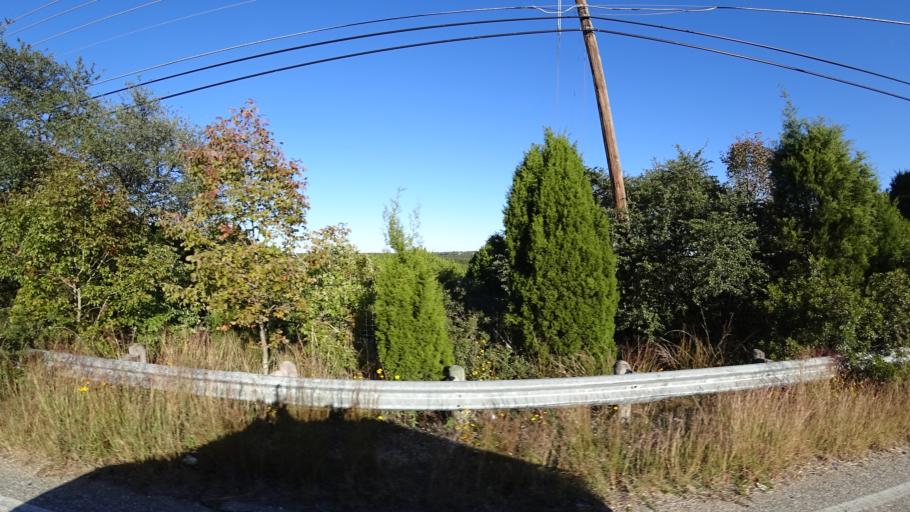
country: US
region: Texas
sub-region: Travis County
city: West Lake Hills
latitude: 30.3638
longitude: -97.8076
